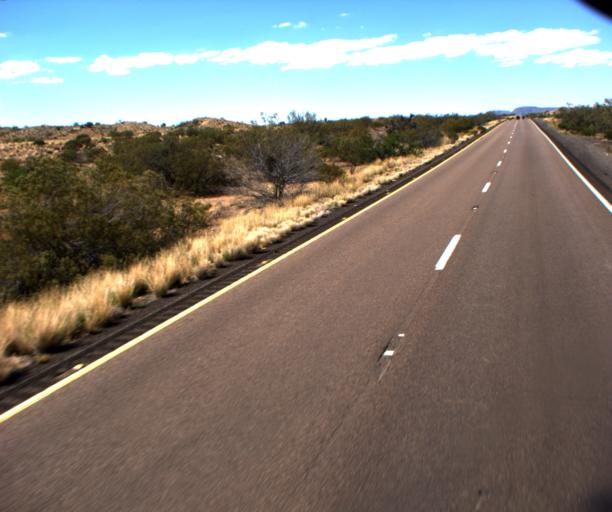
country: US
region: Arizona
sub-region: Mohave County
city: Kingman
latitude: 35.0399
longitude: -113.6645
